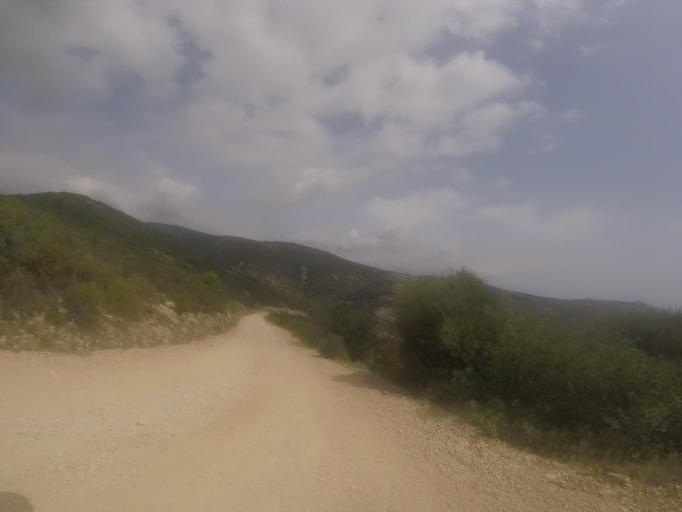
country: ES
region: Valencia
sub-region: Provincia de Castello
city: Peniscola
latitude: 40.3462
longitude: 0.3644
